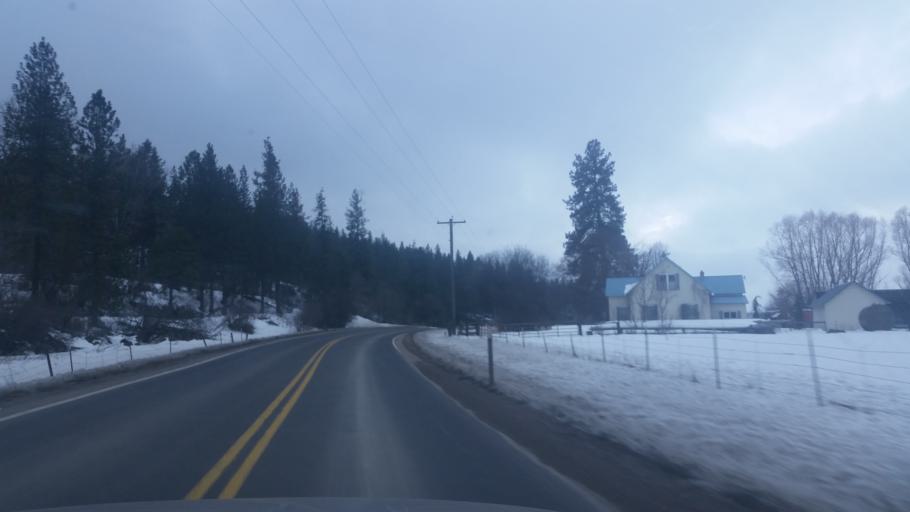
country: US
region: Washington
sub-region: Spokane County
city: Deer Park
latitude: 47.9379
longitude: -117.7704
